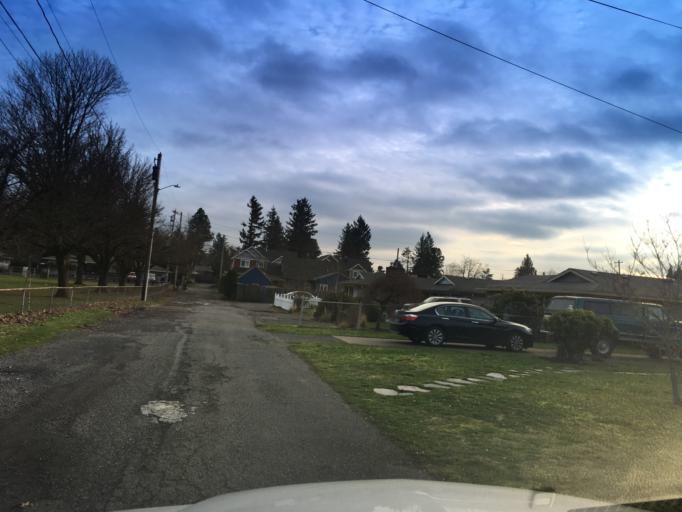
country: US
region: Oregon
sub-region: Multnomah County
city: Lents
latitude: 45.5404
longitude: -122.5476
